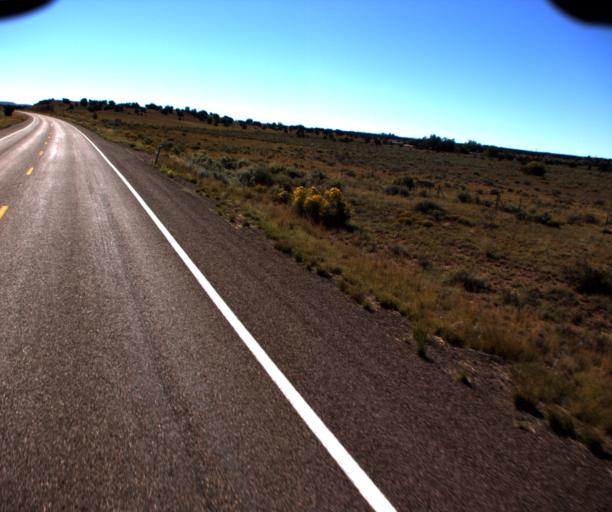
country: US
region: Arizona
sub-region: Apache County
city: Saint Johns
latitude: 34.6084
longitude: -109.6481
